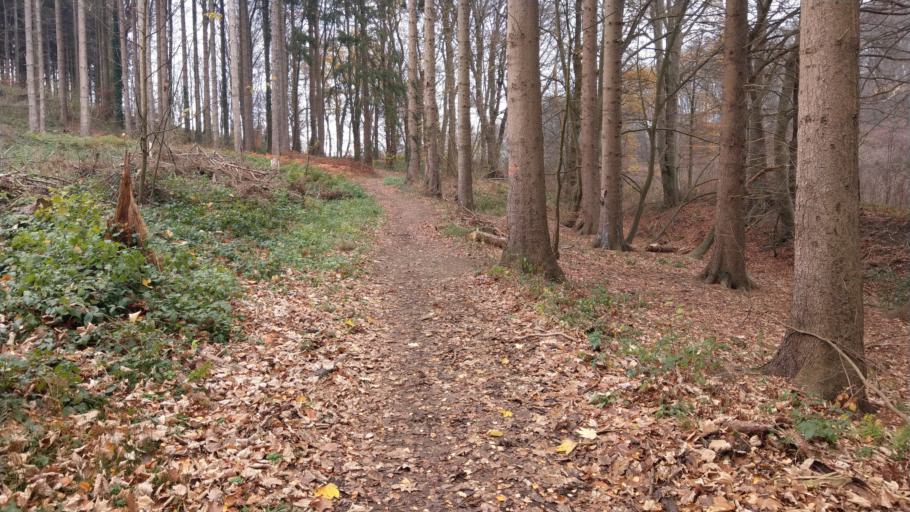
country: DE
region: North Rhine-Westphalia
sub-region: Regierungsbezirk Koln
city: Aachen
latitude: 50.7416
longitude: 6.0573
